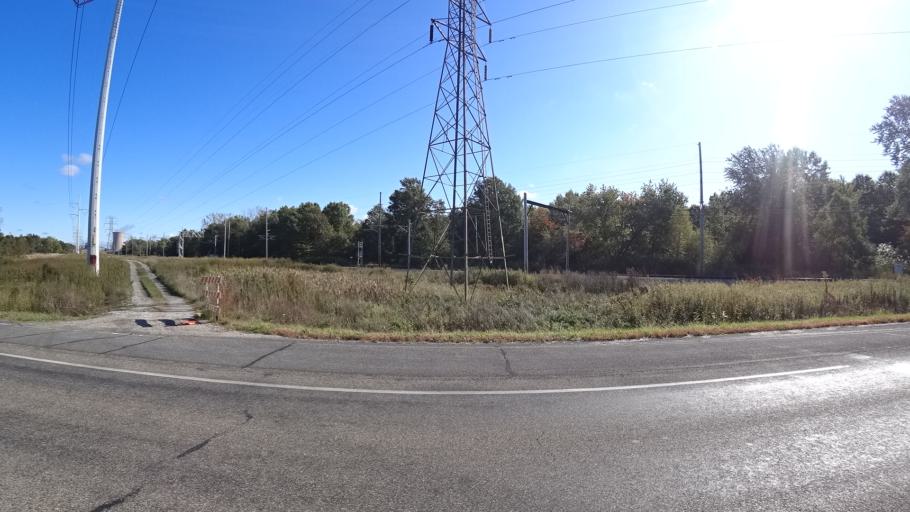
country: US
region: Indiana
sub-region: LaPorte County
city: Michigan City
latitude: 41.6997
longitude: -86.9325
